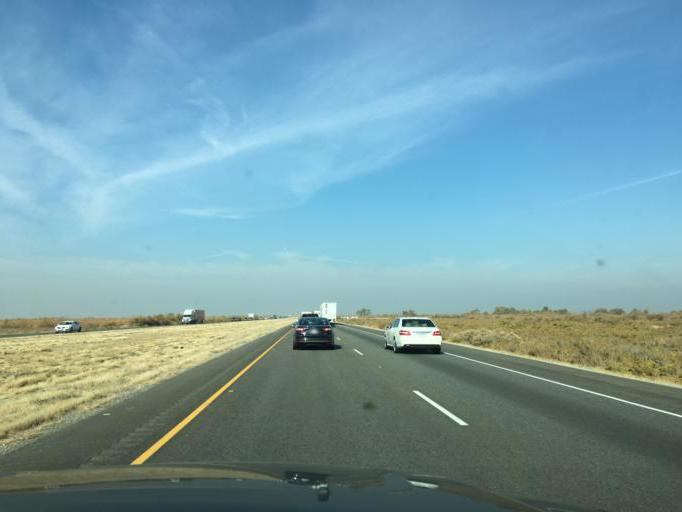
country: US
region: California
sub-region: Kern County
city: Greenfield
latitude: 35.1052
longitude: -119.0482
